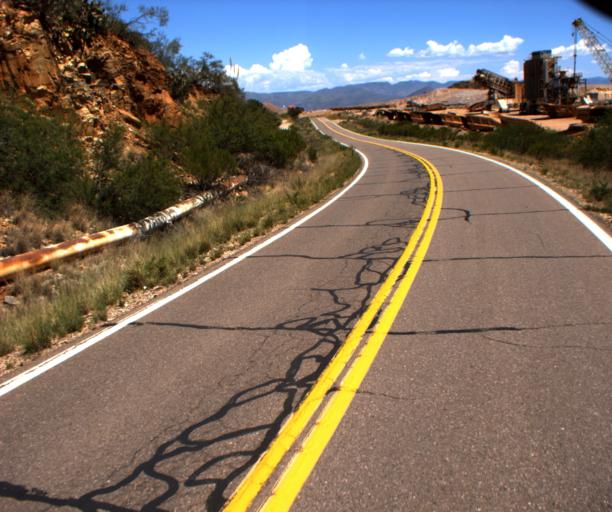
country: US
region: Arizona
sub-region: Greenlee County
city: Morenci
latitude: 33.0703
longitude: -109.3742
